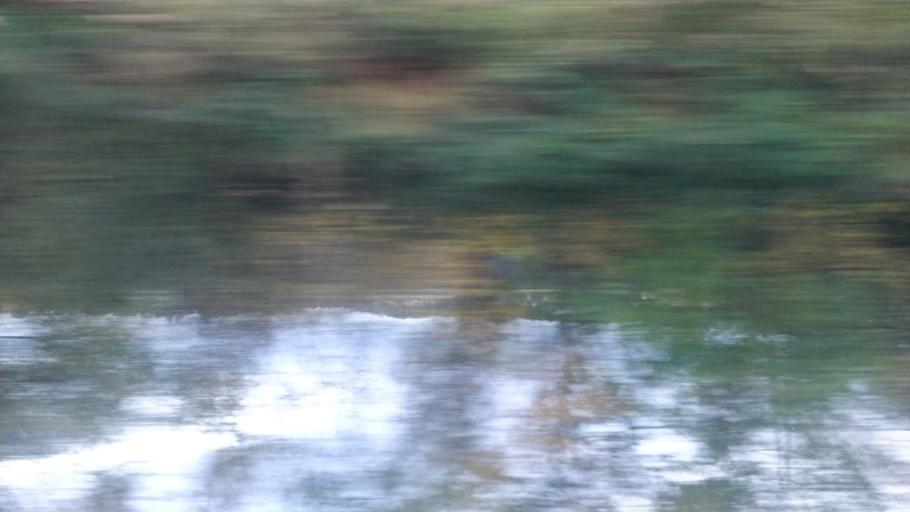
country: GB
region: England
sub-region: Sefton
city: Southport
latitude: 53.6347
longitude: -2.9554
